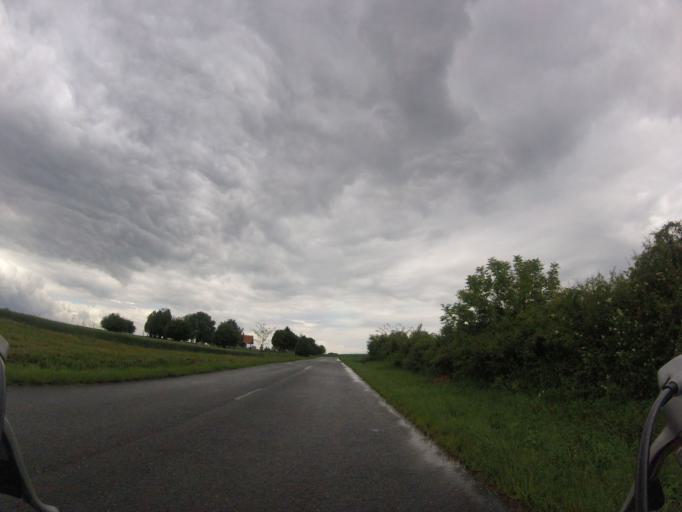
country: HU
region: Baranya
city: Pellerd
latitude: 45.9650
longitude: 18.1925
